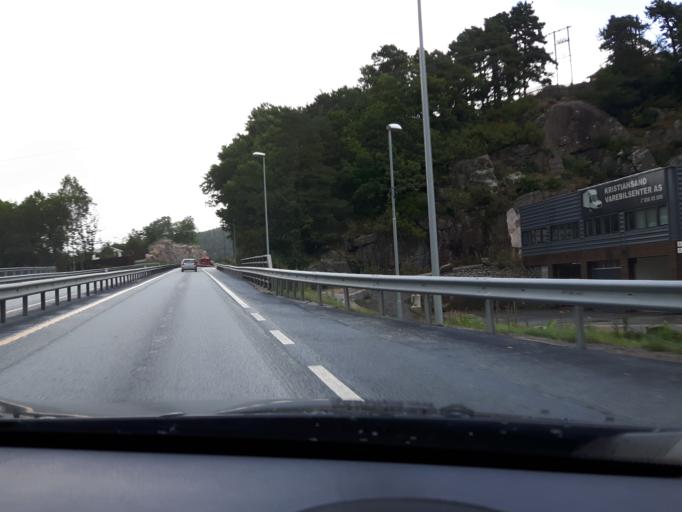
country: NO
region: Vest-Agder
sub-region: Songdalen
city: Nodeland
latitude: 58.1226
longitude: 7.8454
